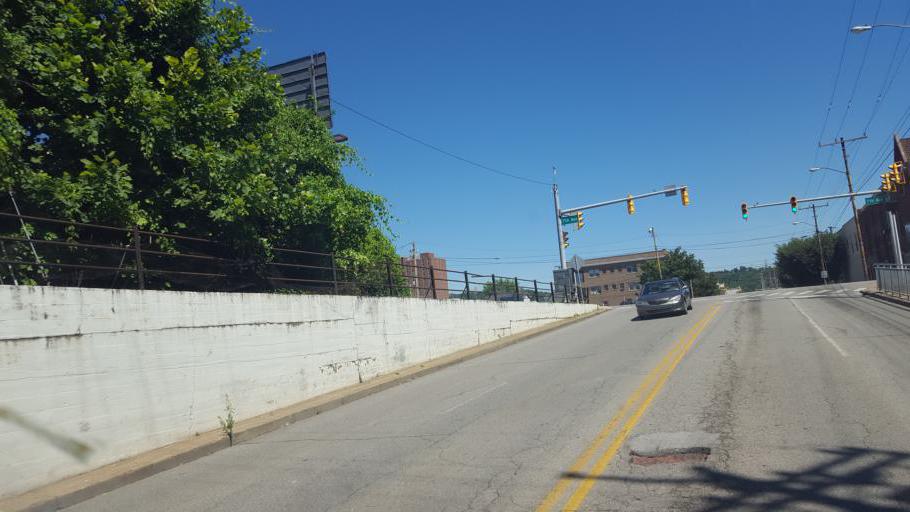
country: US
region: West Virginia
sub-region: Cabell County
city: Huntington
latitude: 38.4200
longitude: -82.4217
